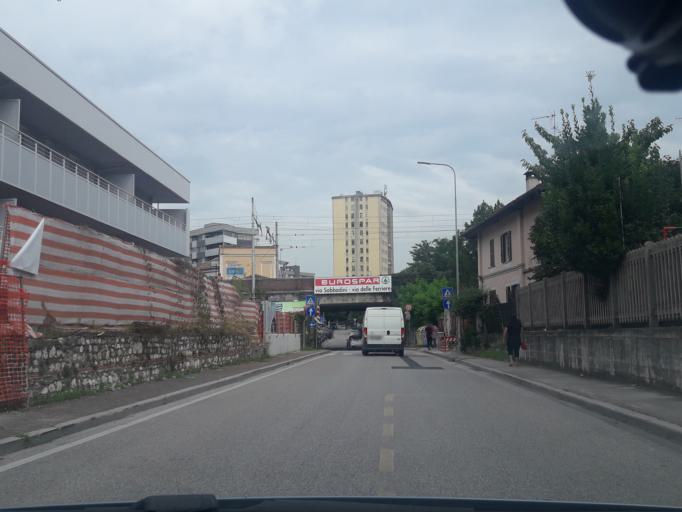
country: IT
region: Friuli Venezia Giulia
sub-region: Provincia di Udine
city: Udine
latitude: 46.0523
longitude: 13.2300
